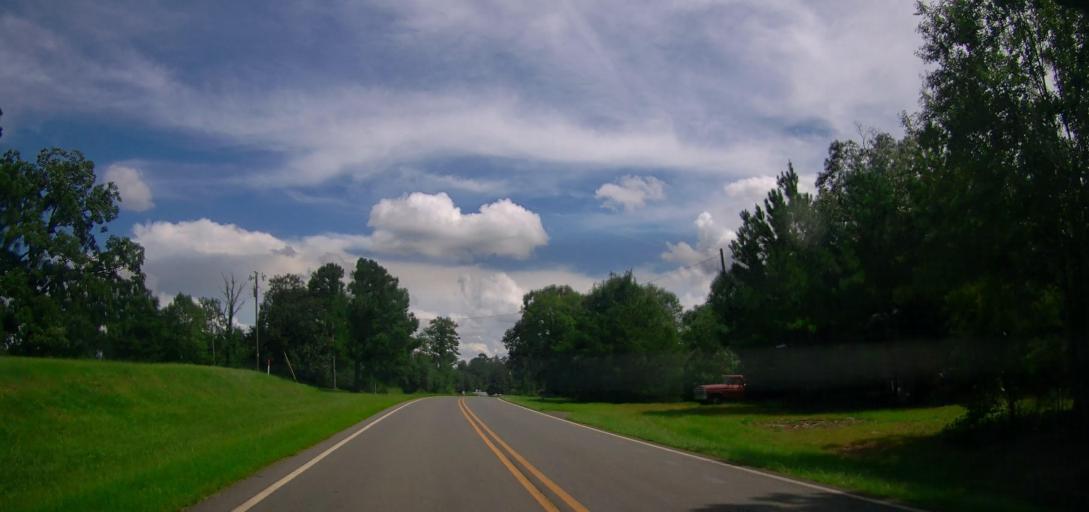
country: US
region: Georgia
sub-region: Taylor County
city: Butler
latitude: 32.5331
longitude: -84.2121
